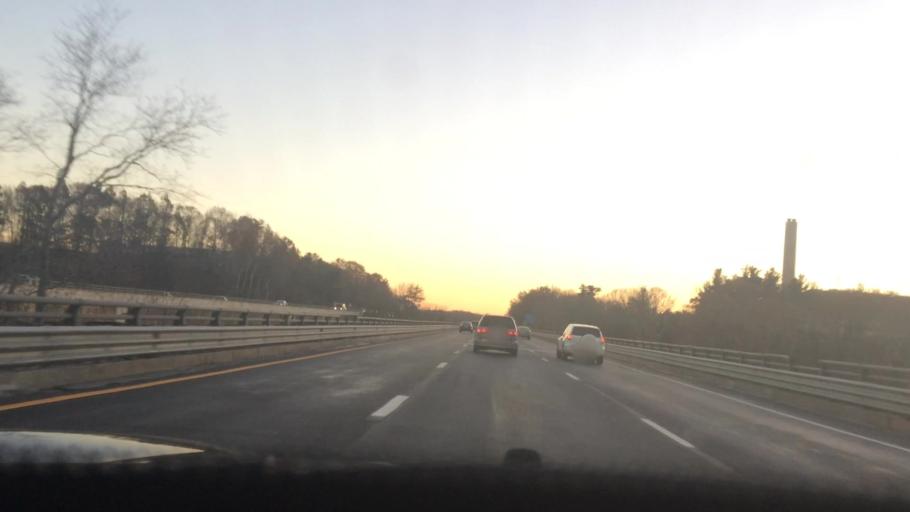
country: US
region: Massachusetts
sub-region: Essex County
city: Haverhill
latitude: 42.7696
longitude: -71.1205
